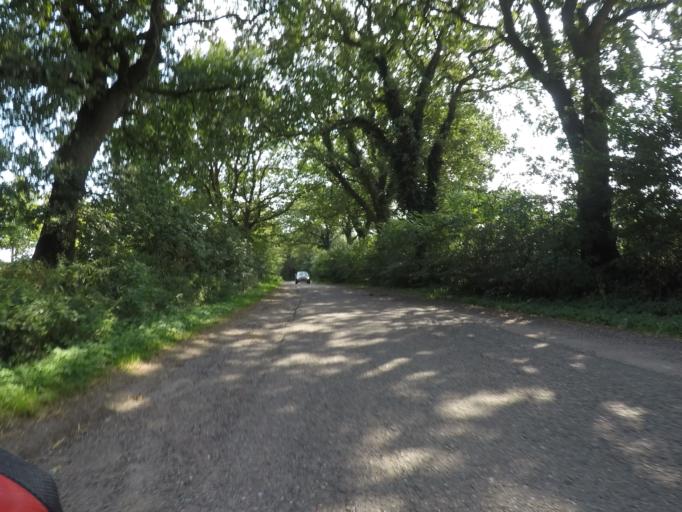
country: DE
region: Schleswig-Holstein
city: Kisdorf
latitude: 53.7983
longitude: 10.0173
